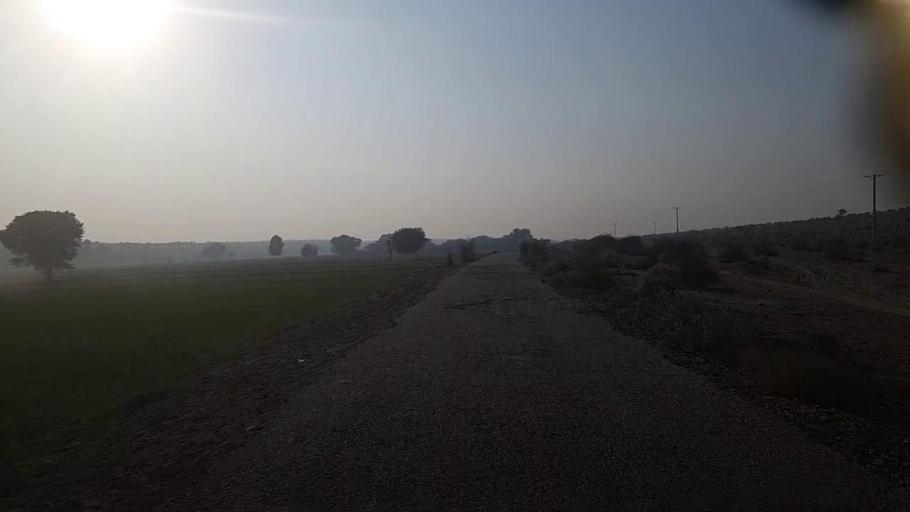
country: PK
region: Sindh
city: Pad Idan
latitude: 26.7136
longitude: 68.4772
